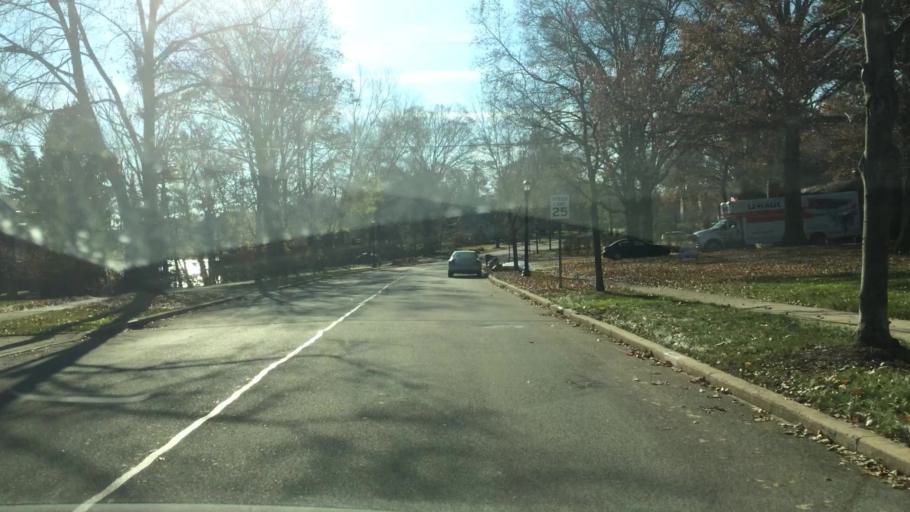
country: US
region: Ohio
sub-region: Summit County
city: Silver Lake
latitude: 41.1588
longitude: -81.4636
